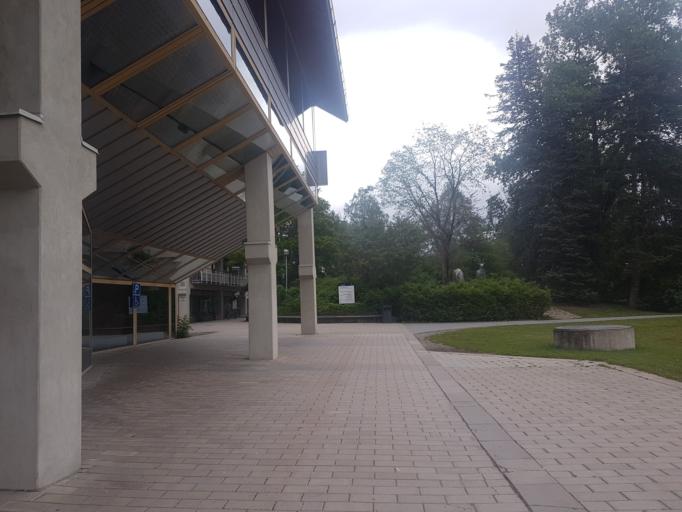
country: SE
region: Stockholm
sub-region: Norrtalje Kommun
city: Bergshamra
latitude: 59.3651
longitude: 18.0592
